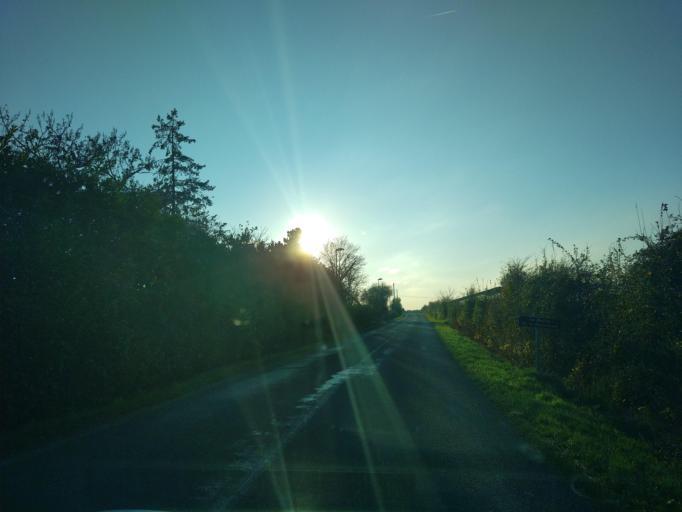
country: FR
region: Pays de la Loire
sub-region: Departement de la Vendee
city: Maillezais
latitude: 46.3391
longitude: -0.7731
